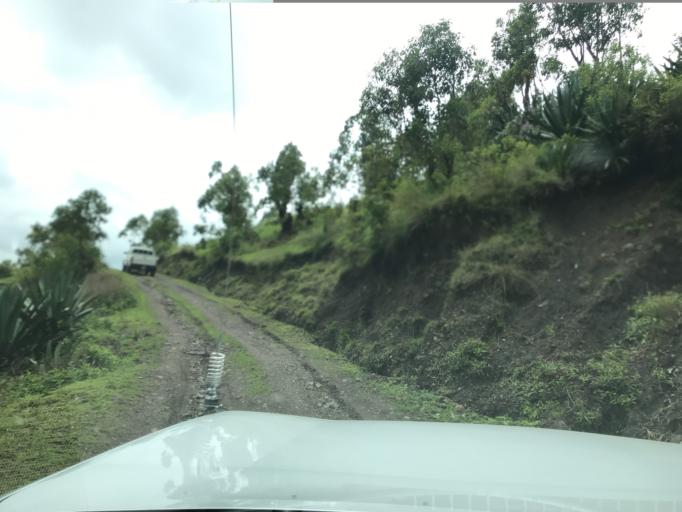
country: TL
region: Ainaro
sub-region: Ainaro
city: Ainaro
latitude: -8.8646
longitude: 125.5552
